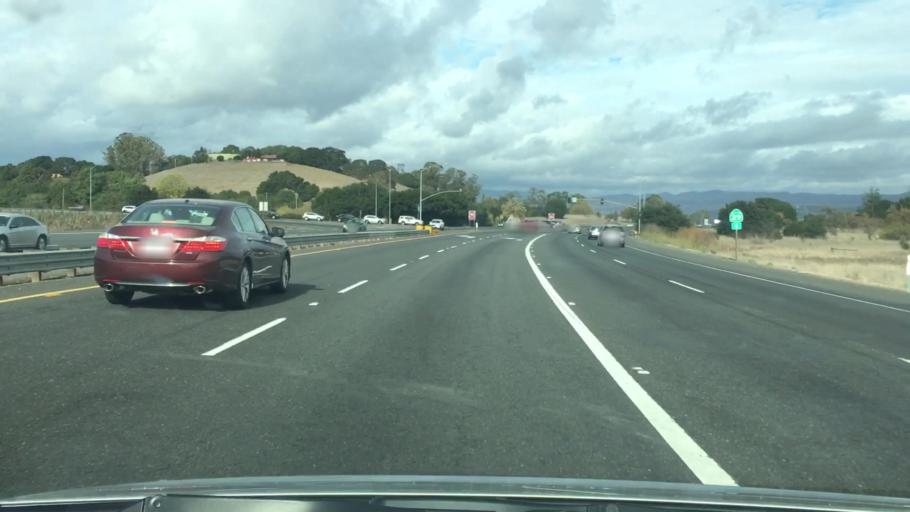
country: US
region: California
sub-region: Napa County
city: Napa
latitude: 38.2561
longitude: -122.3033
